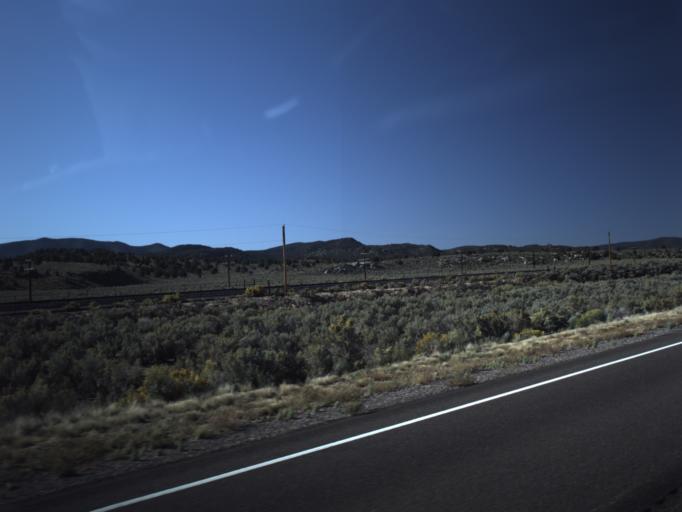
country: US
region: Utah
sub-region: Washington County
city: Enterprise
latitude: 37.7567
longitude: -113.9928
